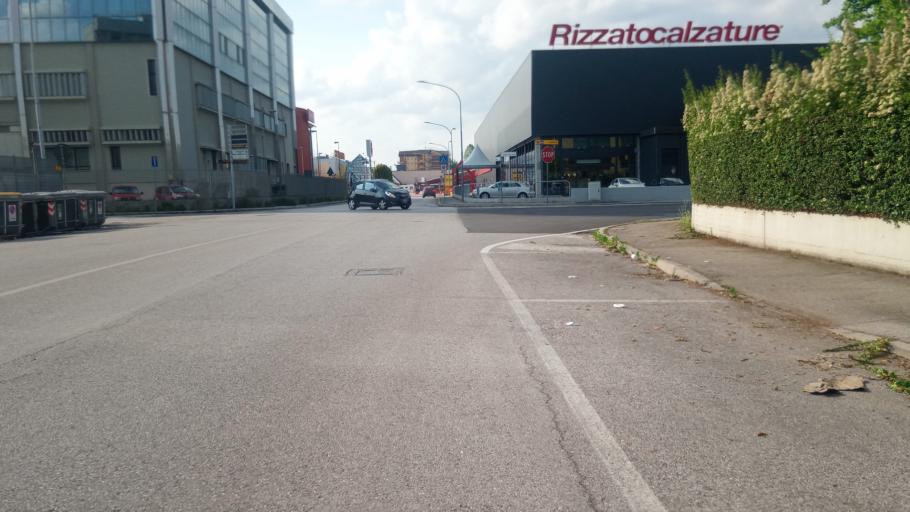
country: IT
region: Veneto
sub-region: Provincia di Padova
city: Padova
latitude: 45.4090
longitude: 11.9089
